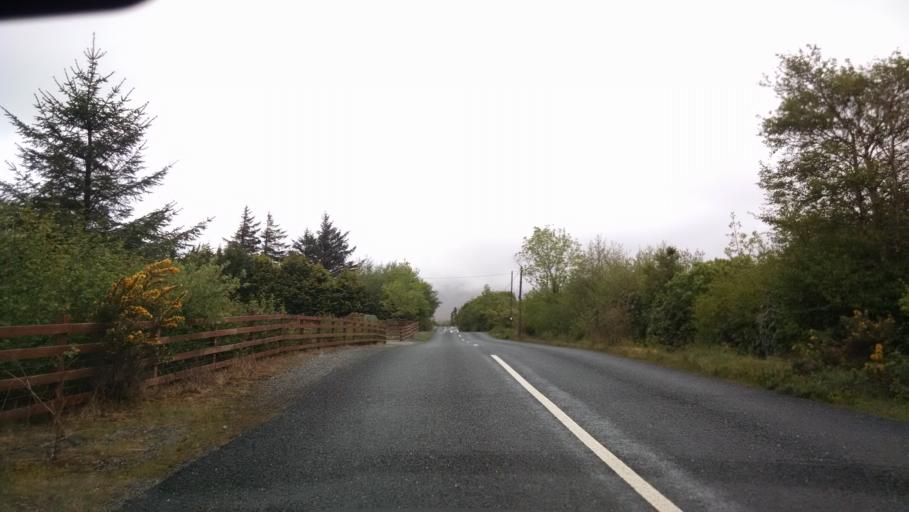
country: IE
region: Connaught
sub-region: County Galway
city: Clifden
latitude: 53.4829
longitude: -9.7409
